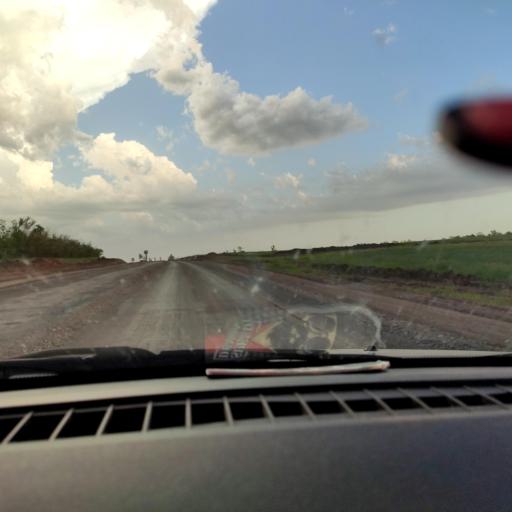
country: RU
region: Orenburg
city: Sakmara
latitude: 52.1850
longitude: 55.2946
